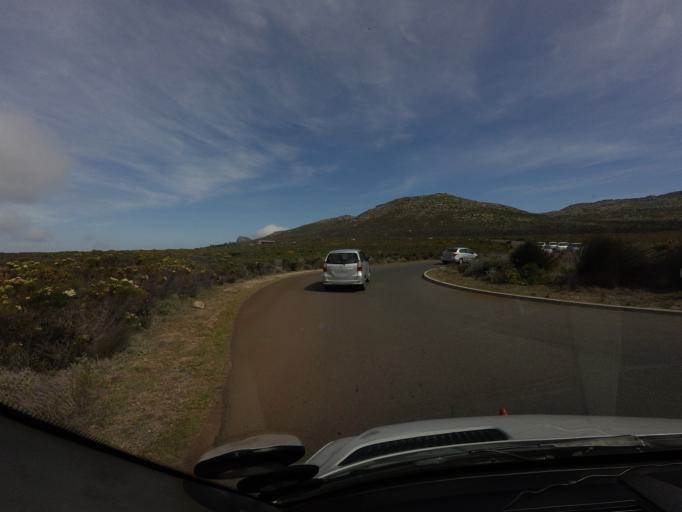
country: ZA
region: Western Cape
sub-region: City of Cape Town
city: Retreat
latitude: -34.2614
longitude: 18.4581
